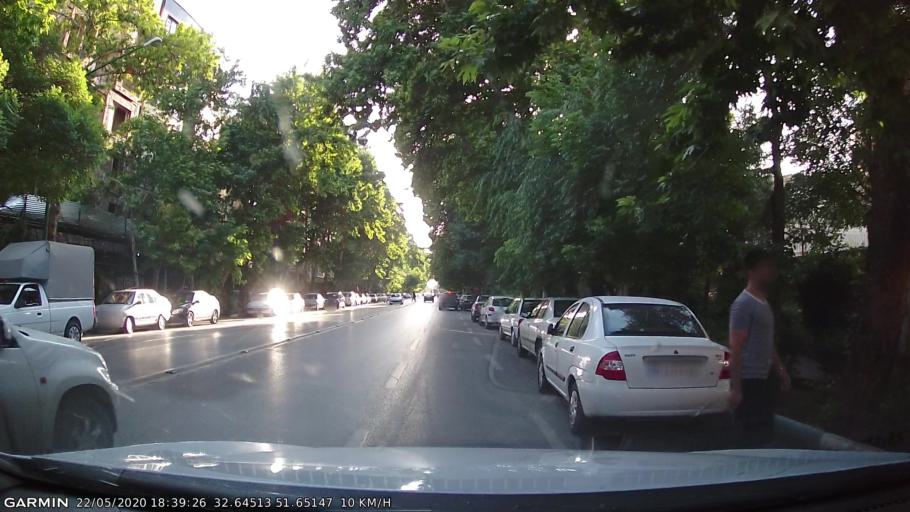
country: IR
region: Isfahan
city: Isfahan
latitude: 32.6440
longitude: 51.6520
